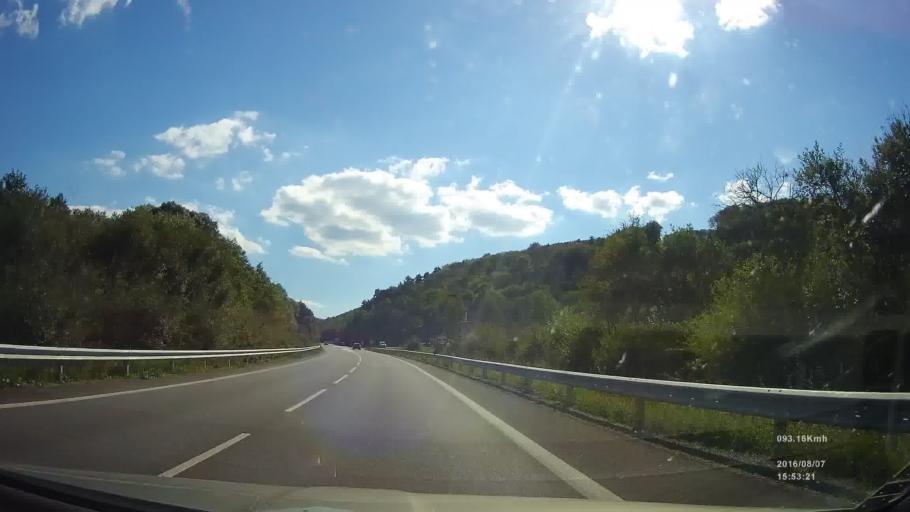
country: SK
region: Presovsky
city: Giraltovce
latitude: 49.1003
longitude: 21.4539
